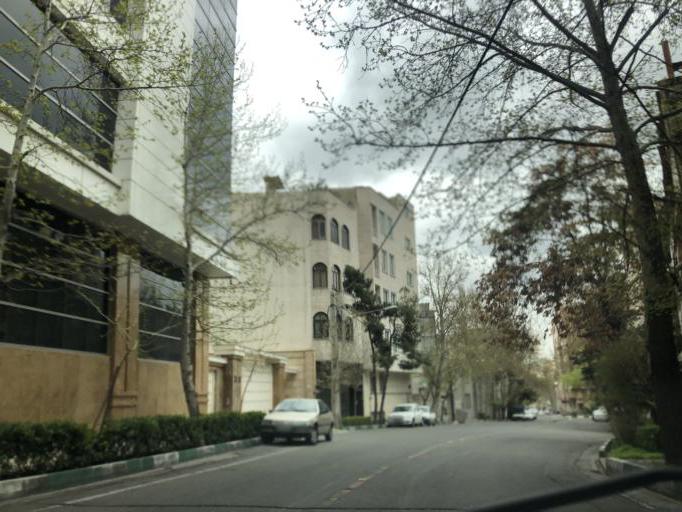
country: IR
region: Tehran
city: Tajrish
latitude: 35.7806
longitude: 51.4653
